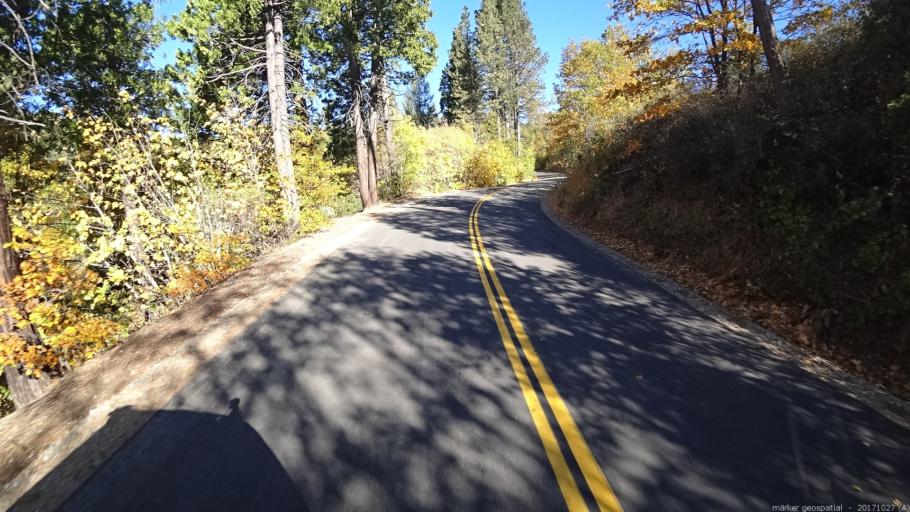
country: US
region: California
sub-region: Shasta County
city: Burney
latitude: 40.8580
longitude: -121.9109
